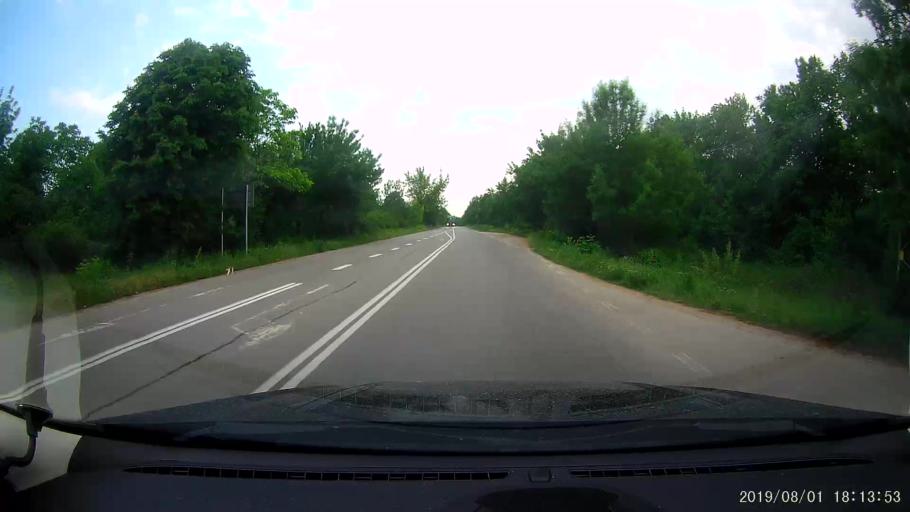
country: BG
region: Silistra
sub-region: Obshtina Dulovo
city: Dulovo
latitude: 43.7803
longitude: 27.1308
